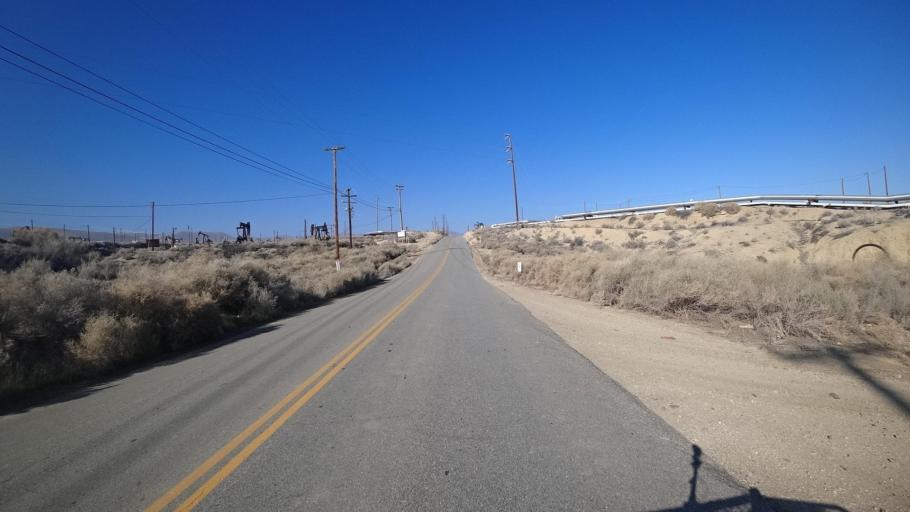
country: US
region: California
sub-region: Kern County
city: Taft Heights
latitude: 35.2240
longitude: -119.6221
